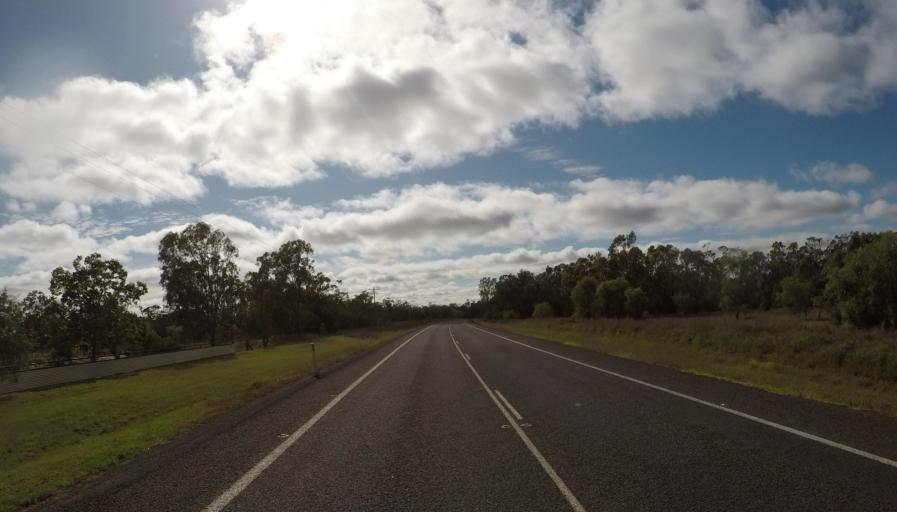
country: AU
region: Queensland
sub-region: Maranoa
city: Roma
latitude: -26.5797
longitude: 148.9567
